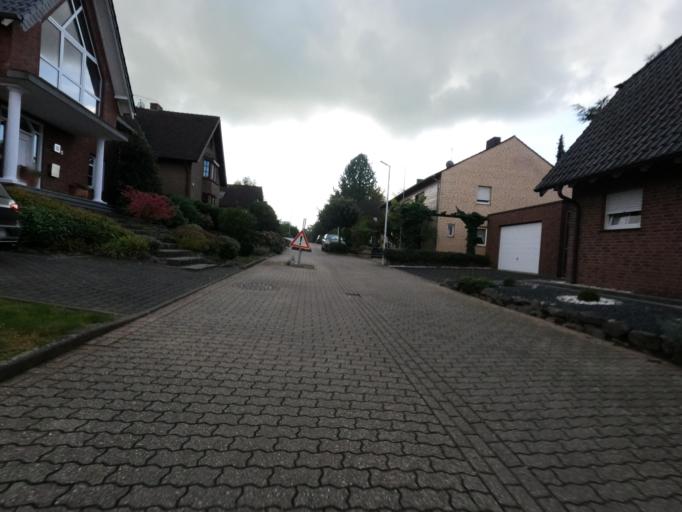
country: DE
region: North Rhine-Westphalia
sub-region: Regierungsbezirk Koln
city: Linnich
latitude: 50.9998
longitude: 6.2854
